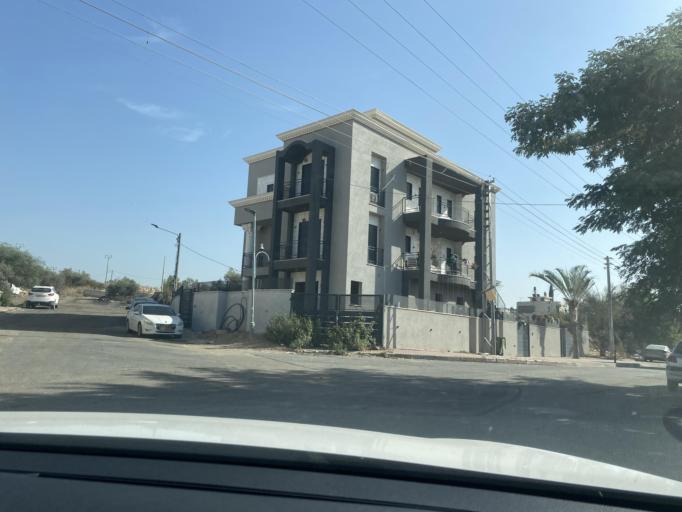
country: IL
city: Oranit
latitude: 32.1327
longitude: 34.9745
